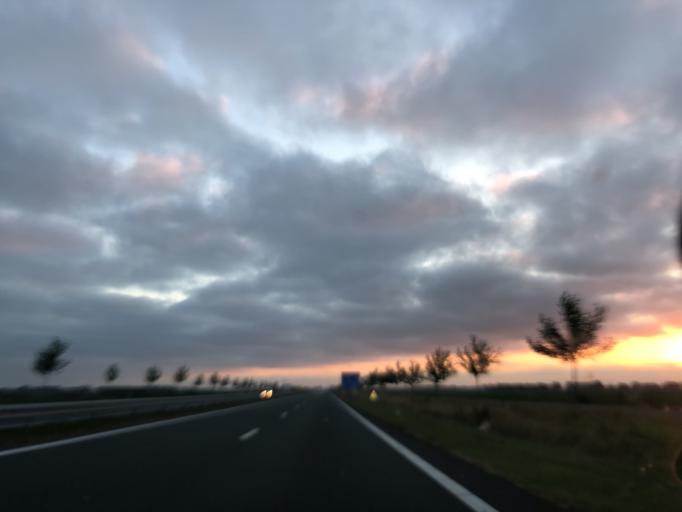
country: NL
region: Groningen
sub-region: Gemeente Veendam
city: Veendam
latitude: 53.0663
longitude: 6.8753
